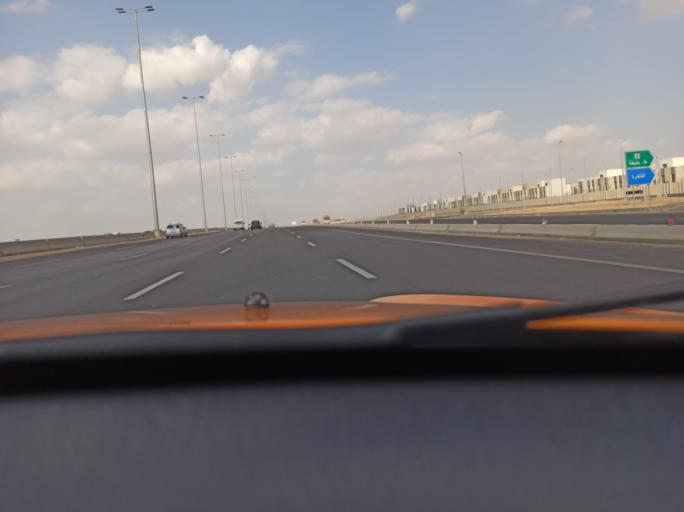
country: EG
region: Eastern Province
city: Bilbays
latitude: 30.1971
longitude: 31.6568
